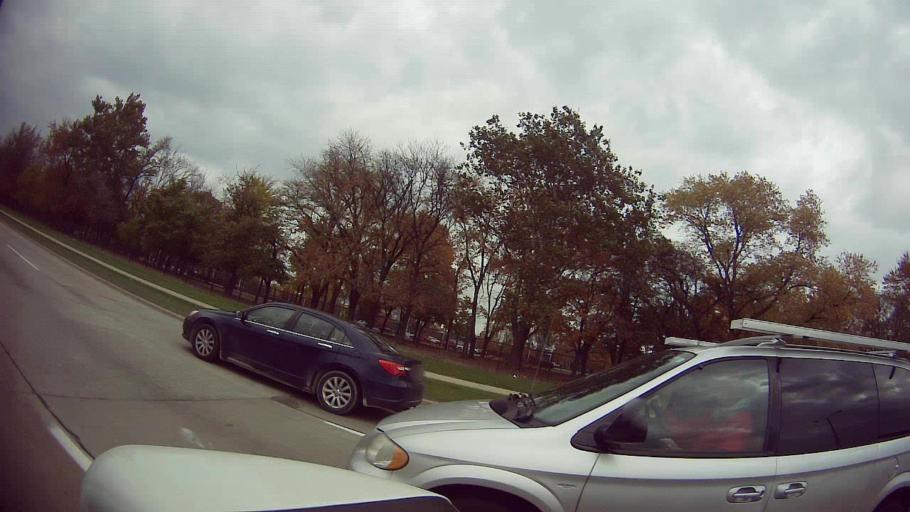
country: US
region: Michigan
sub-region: Macomb County
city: Center Line
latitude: 42.5156
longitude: -83.0466
